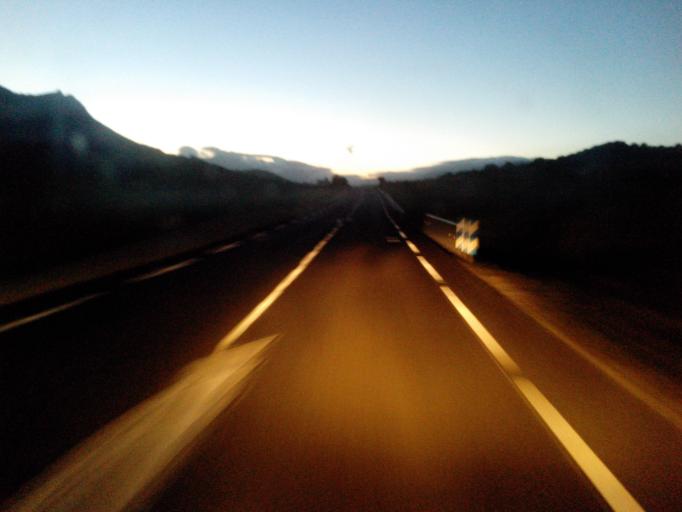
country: FR
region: Languedoc-Roussillon
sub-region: Departement des Pyrenees-Orientales
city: Saint-Paul-de-Fenouillet
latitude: 42.8147
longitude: 2.5570
